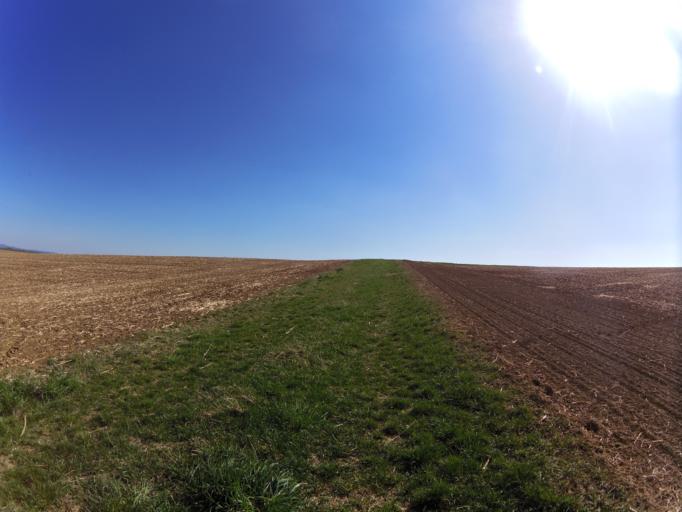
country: DE
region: Bavaria
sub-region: Regierungsbezirk Unterfranken
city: Winterhausen
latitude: 49.6850
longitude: 10.0014
